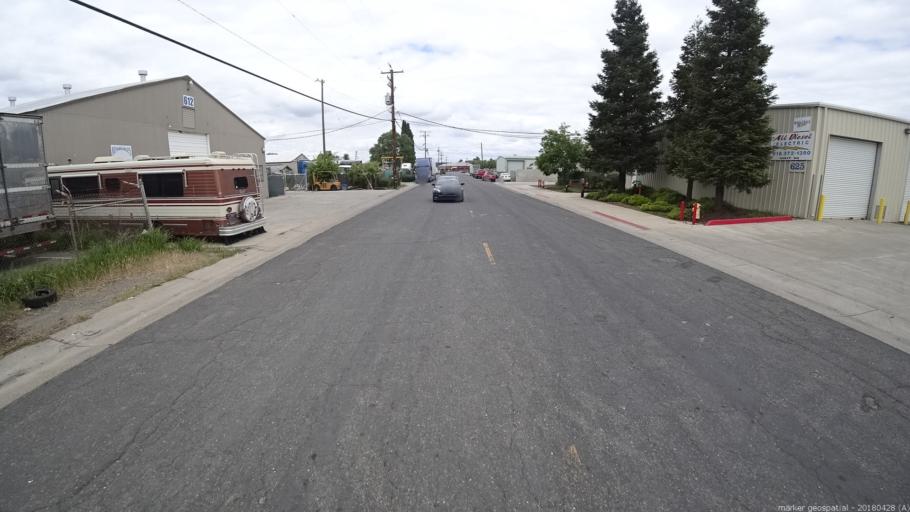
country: US
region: California
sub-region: Yolo County
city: West Sacramento
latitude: 38.5815
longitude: -121.5527
